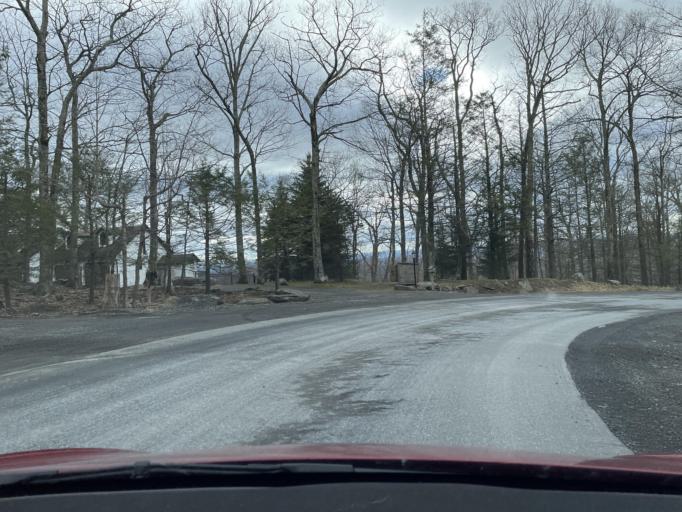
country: US
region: New York
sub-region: Ulster County
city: Woodstock
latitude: 42.0618
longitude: -74.1197
